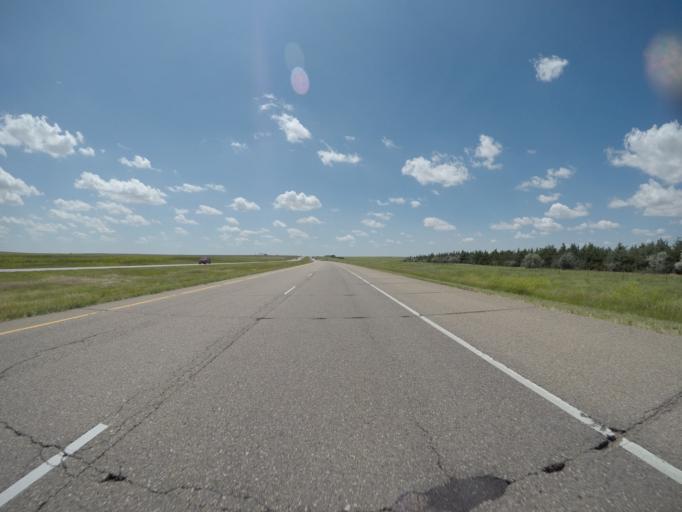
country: US
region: Colorado
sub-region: Lincoln County
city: Hugo
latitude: 39.2932
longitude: -102.8820
